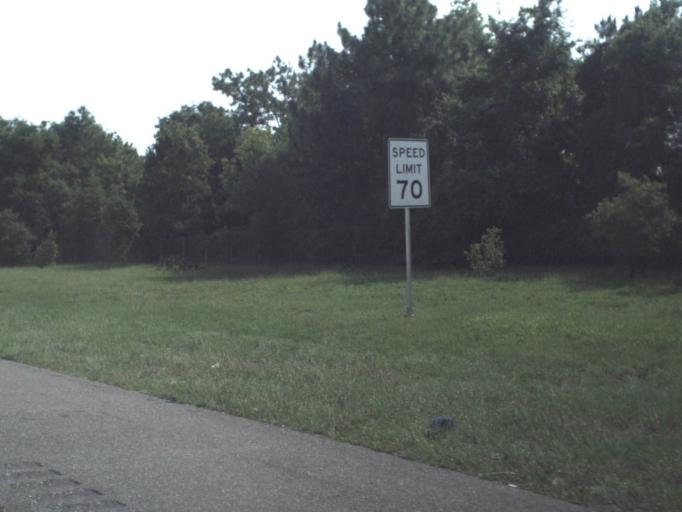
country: US
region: Florida
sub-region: Duval County
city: Jacksonville
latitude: 30.4244
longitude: -81.6563
